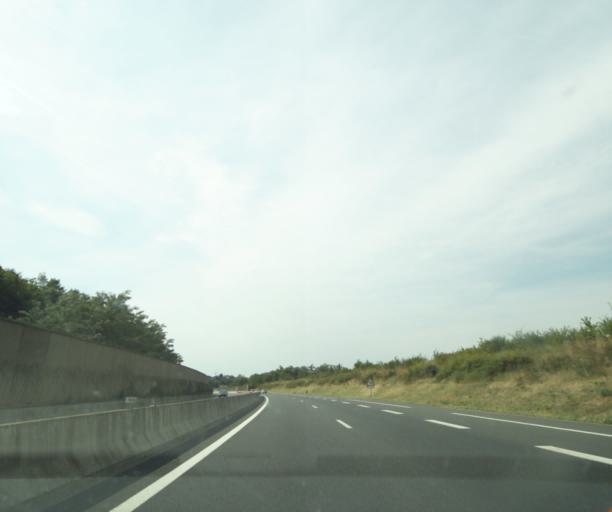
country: FR
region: Centre
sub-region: Departement d'Indre-et-Loire
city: Saint-Cyr-sur-Loire
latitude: 47.4034
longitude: 0.6440
